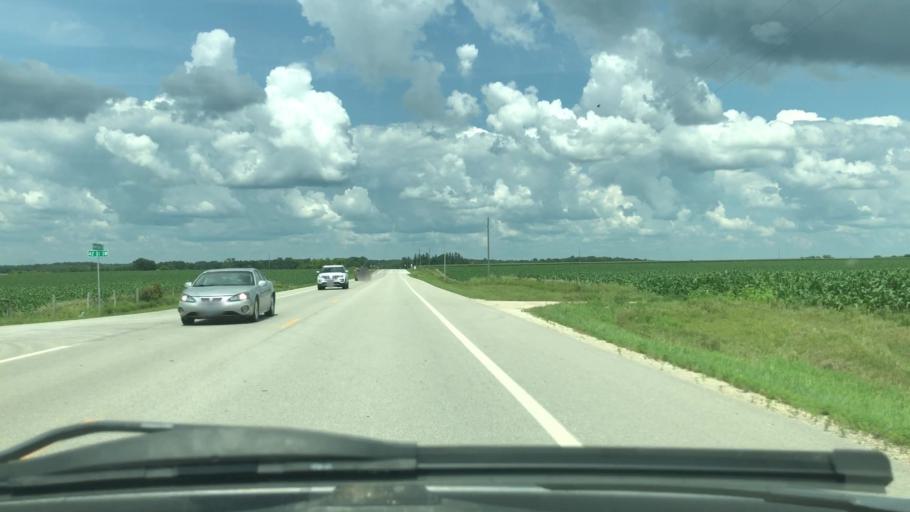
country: US
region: Minnesota
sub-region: Olmsted County
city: Rochester
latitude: 43.9602
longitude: -92.5183
